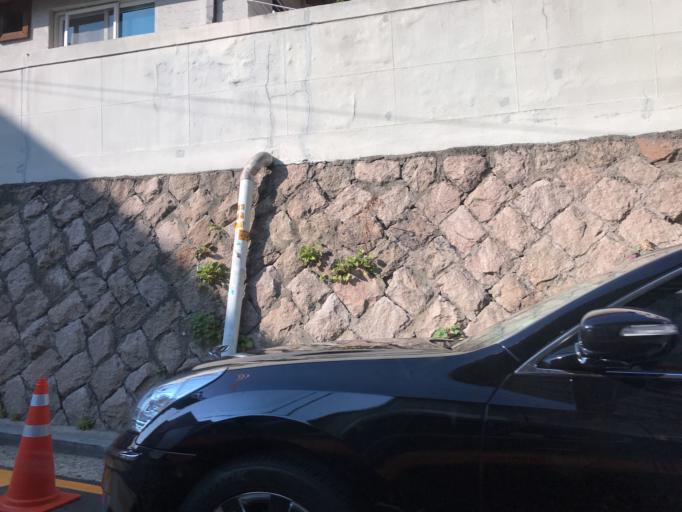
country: KR
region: Seoul
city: Seoul
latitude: 37.5714
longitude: 126.9716
